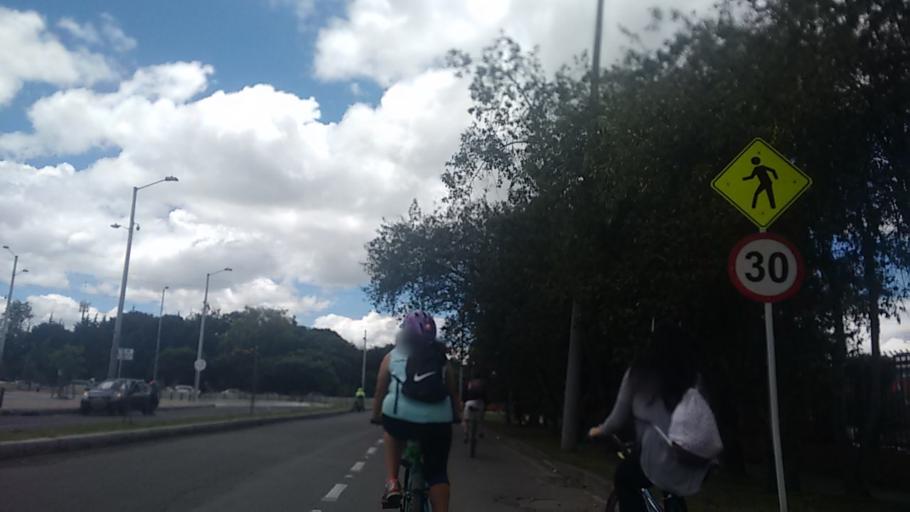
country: CO
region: Cundinamarca
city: Cota
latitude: 4.7709
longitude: -74.0419
